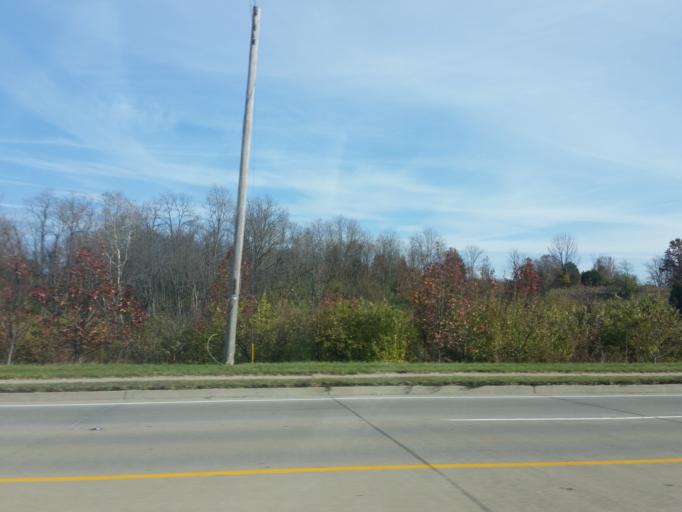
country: US
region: Kentucky
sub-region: Campbell County
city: Alexandria
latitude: 38.9474
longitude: -84.3938
